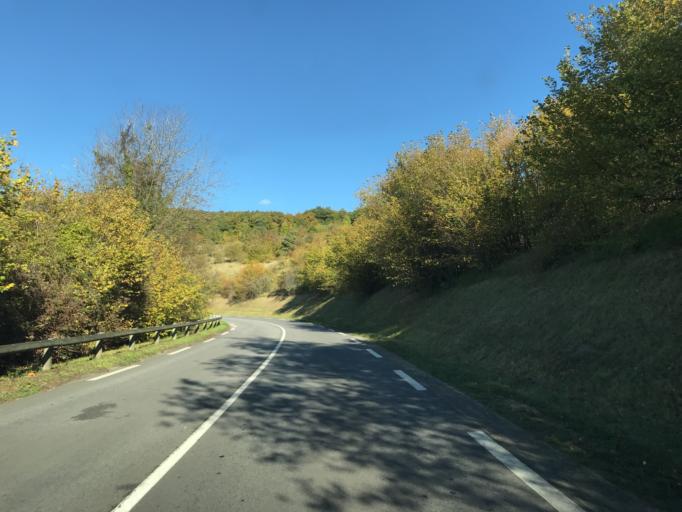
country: FR
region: Haute-Normandie
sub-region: Departement de l'Eure
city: Saint-Aubin-sur-Gaillon
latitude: 49.0990
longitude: 1.2915
